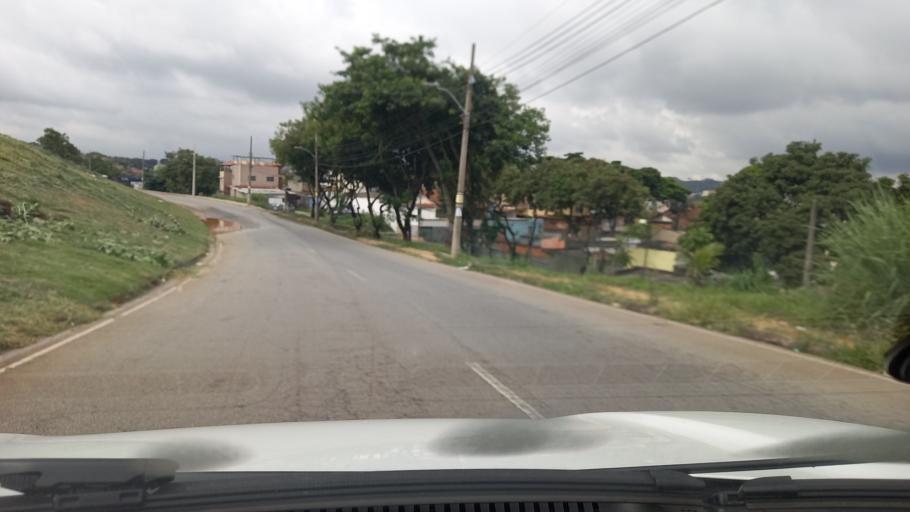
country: BR
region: Minas Gerais
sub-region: Belo Horizonte
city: Belo Horizonte
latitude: -19.9097
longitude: -43.9946
